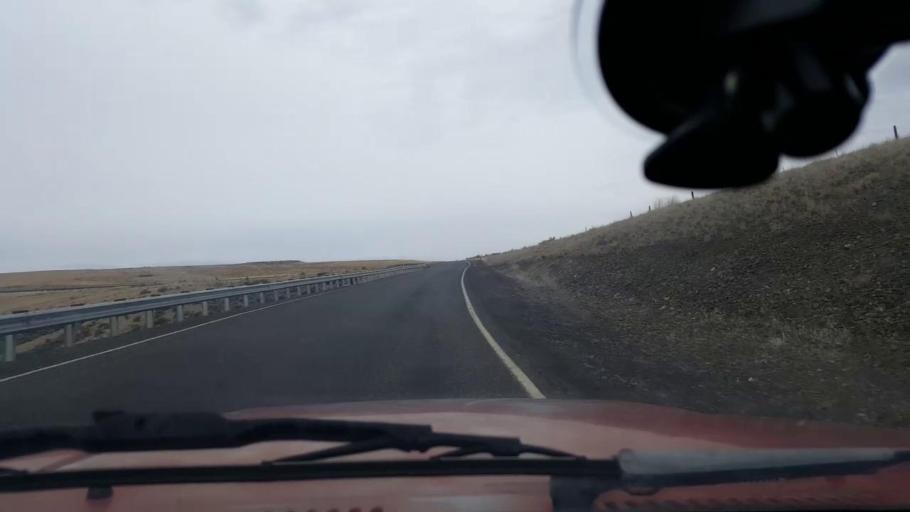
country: US
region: Washington
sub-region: Asotin County
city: Clarkston Heights-Vineland
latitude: 46.3352
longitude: -117.3028
